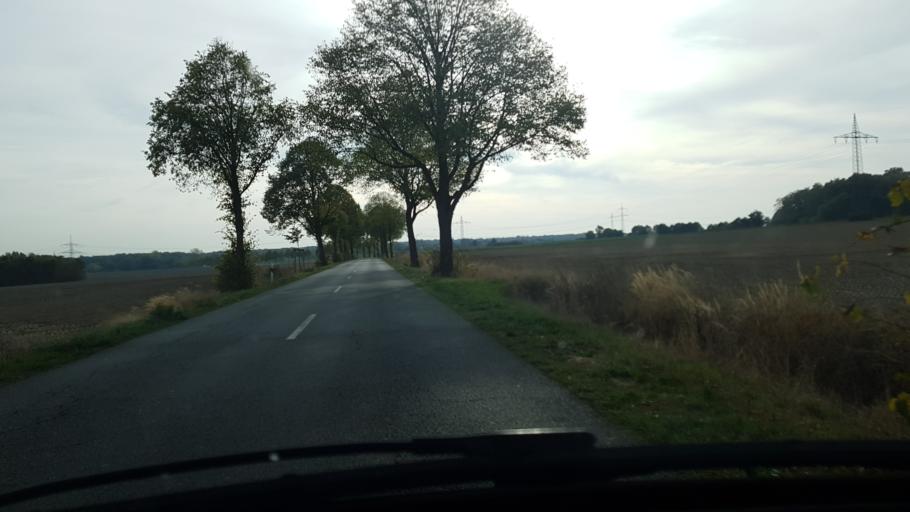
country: DE
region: Lower Saxony
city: Lehre
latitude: 52.3835
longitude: 10.6832
